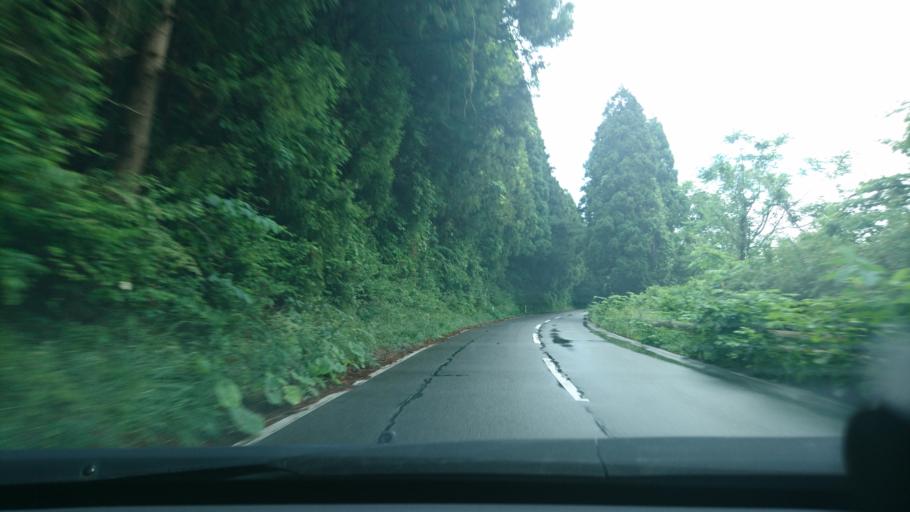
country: JP
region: Miyagi
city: Wakuya
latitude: 38.6696
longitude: 141.2829
